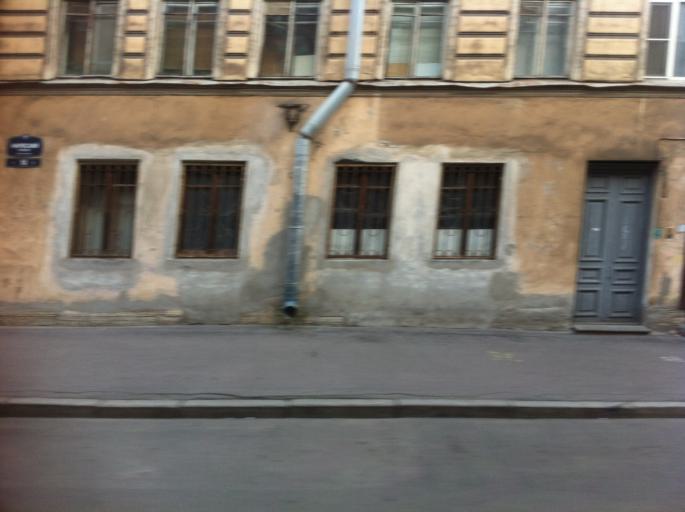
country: RU
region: St.-Petersburg
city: Admiralteisky
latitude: 59.9046
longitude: 30.2741
